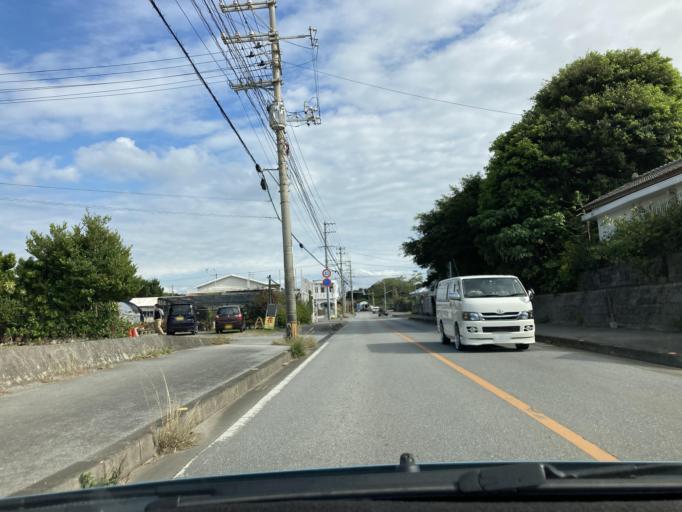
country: JP
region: Okinawa
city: Nago
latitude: 26.6920
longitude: 127.9585
